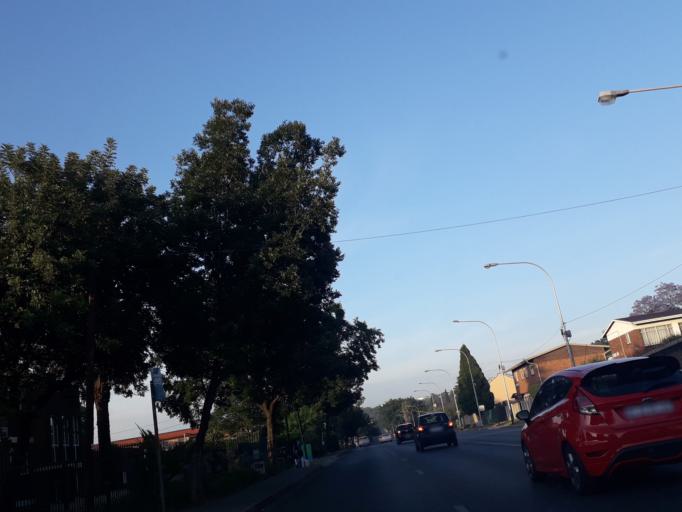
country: ZA
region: Gauteng
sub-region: City of Johannesburg Metropolitan Municipality
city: Modderfontein
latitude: -26.1276
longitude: 28.1049
